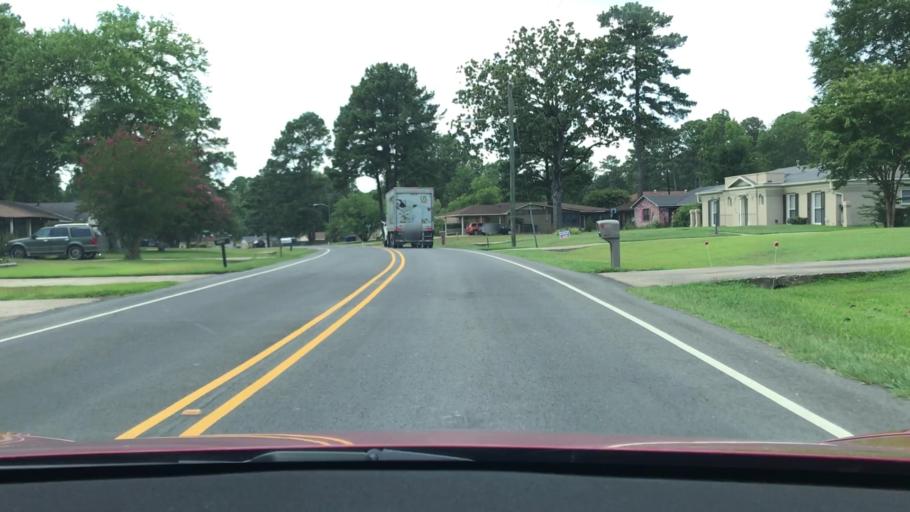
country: US
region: Louisiana
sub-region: De Soto Parish
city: Stonewall
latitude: 32.3934
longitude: -93.7971
